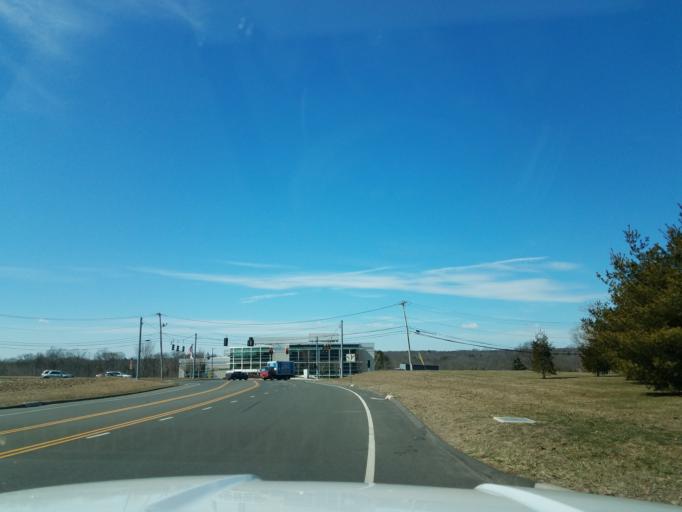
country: US
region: Connecticut
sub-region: New Haven County
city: Woodmont
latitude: 41.2580
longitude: -72.9991
